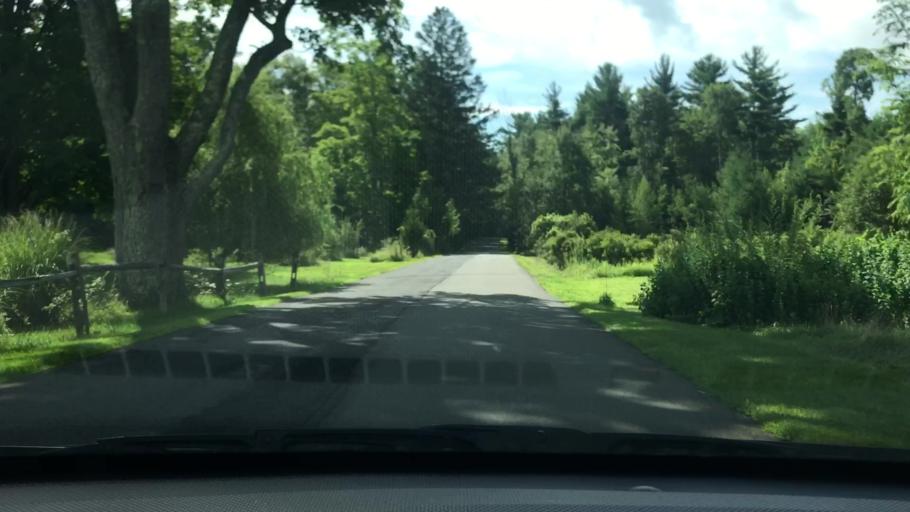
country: US
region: New York
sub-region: Ulster County
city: Shokan
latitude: 41.9602
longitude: -74.2798
